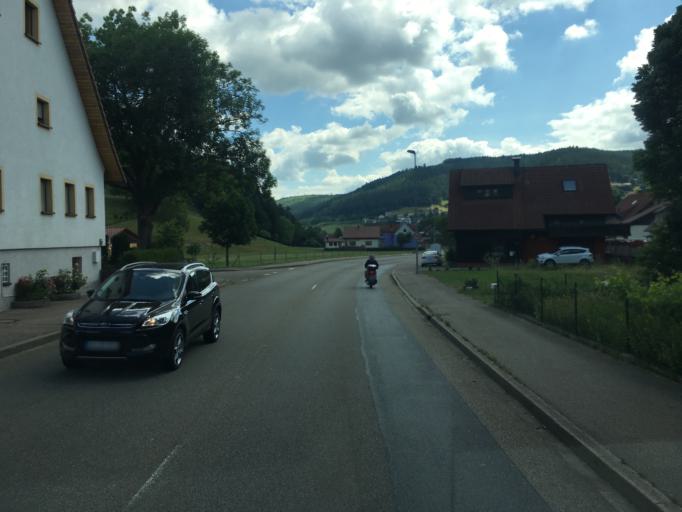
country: DE
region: Baden-Wuerttemberg
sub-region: Karlsruhe Region
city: Baiersbronn
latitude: 48.5096
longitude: 8.3620
